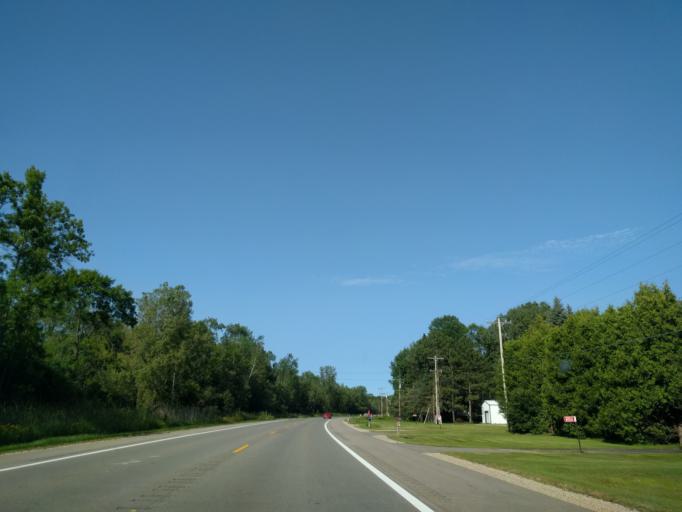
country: US
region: Michigan
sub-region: Menominee County
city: Menominee
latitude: 45.1672
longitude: -87.5862
